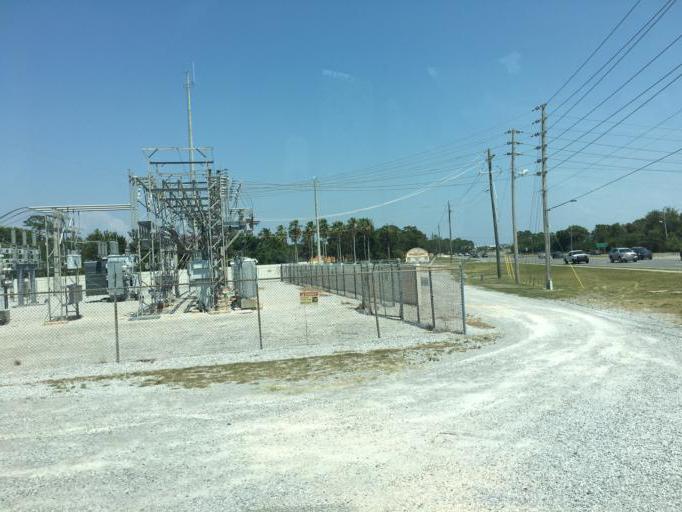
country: US
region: Florida
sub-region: Bay County
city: Laguna Beach
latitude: 30.2275
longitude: -85.8786
